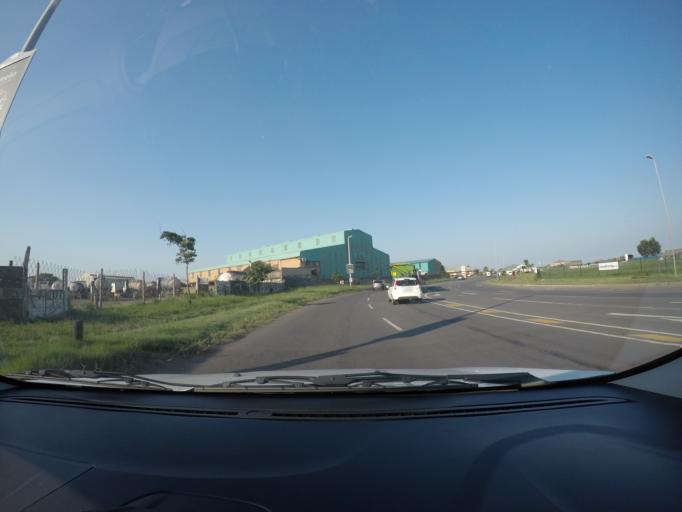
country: ZA
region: KwaZulu-Natal
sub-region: uThungulu District Municipality
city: Richards Bay
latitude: -28.7534
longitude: 32.0261
